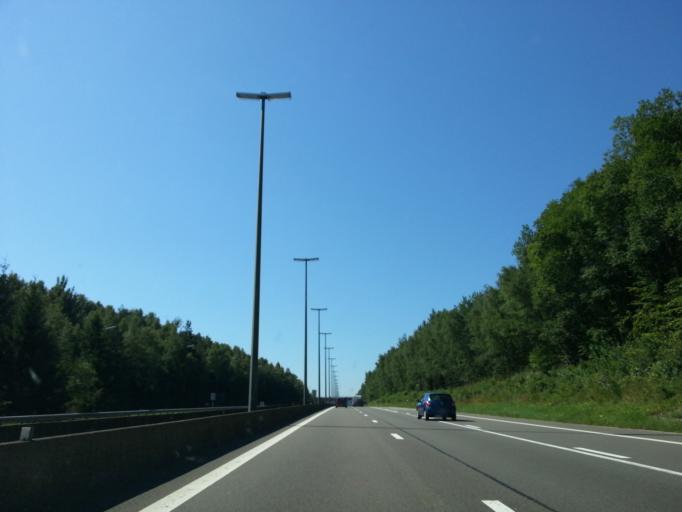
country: BE
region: Wallonia
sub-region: Province de Liege
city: Malmedy
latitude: 50.4085
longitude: 5.9881
